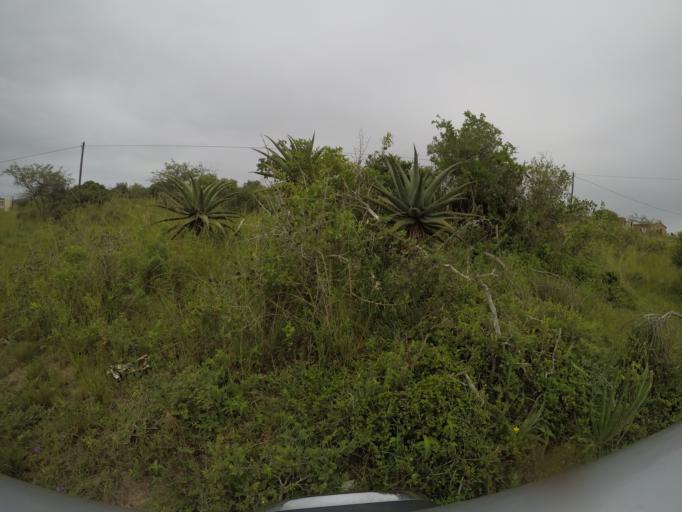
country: ZA
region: KwaZulu-Natal
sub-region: uThungulu District Municipality
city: Empangeni
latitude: -28.6074
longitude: 31.8396
